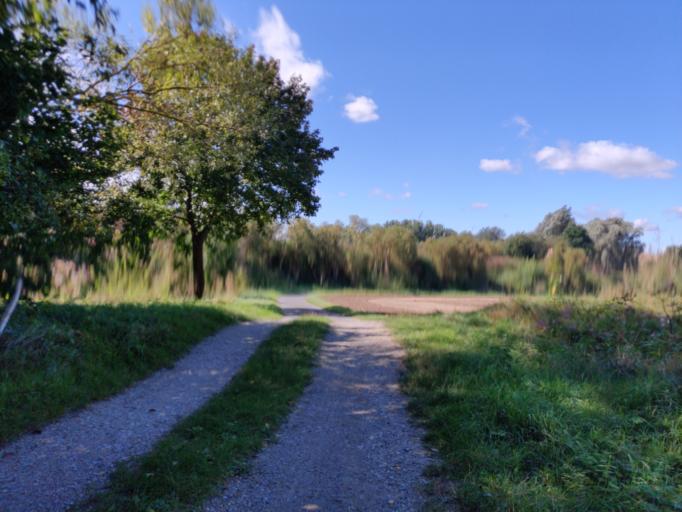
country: DE
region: Lower Saxony
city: Baddeckenstedt
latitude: 52.0903
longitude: 10.2110
